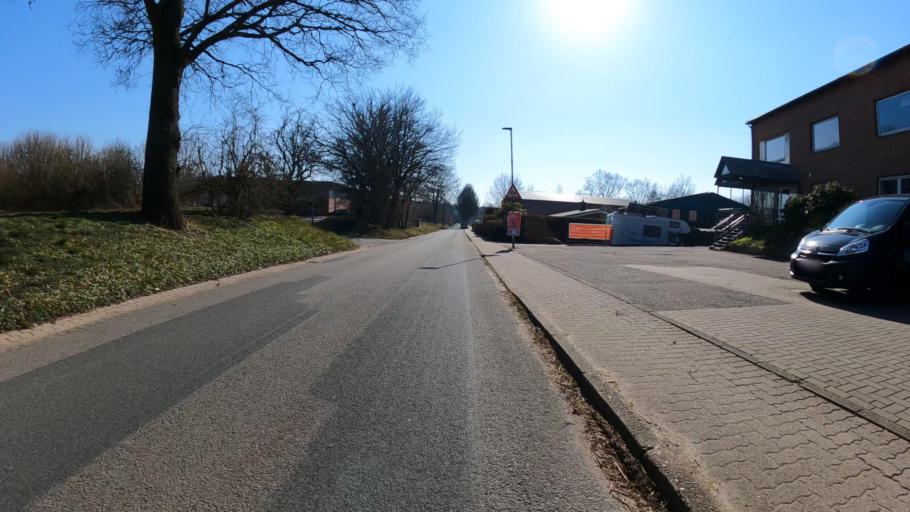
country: DE
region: Lower Saxony
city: Bendestorf
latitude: 53.3619
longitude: 9.9277
